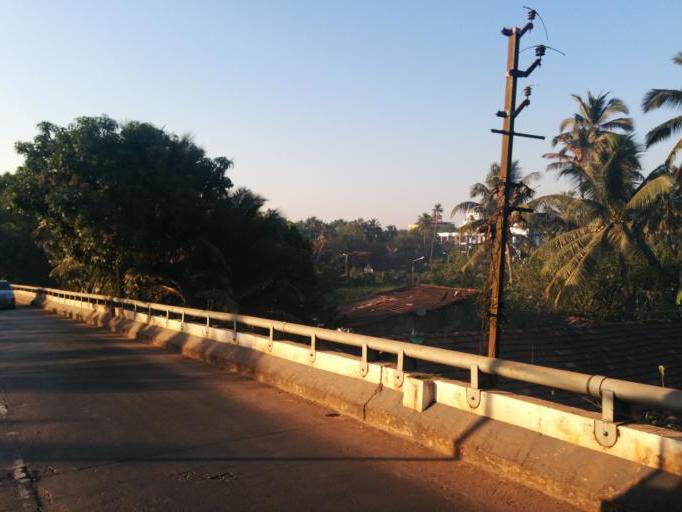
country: IN
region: Goa
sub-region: South Goa
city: Madgaon
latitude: 15.2679
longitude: 73.9597
